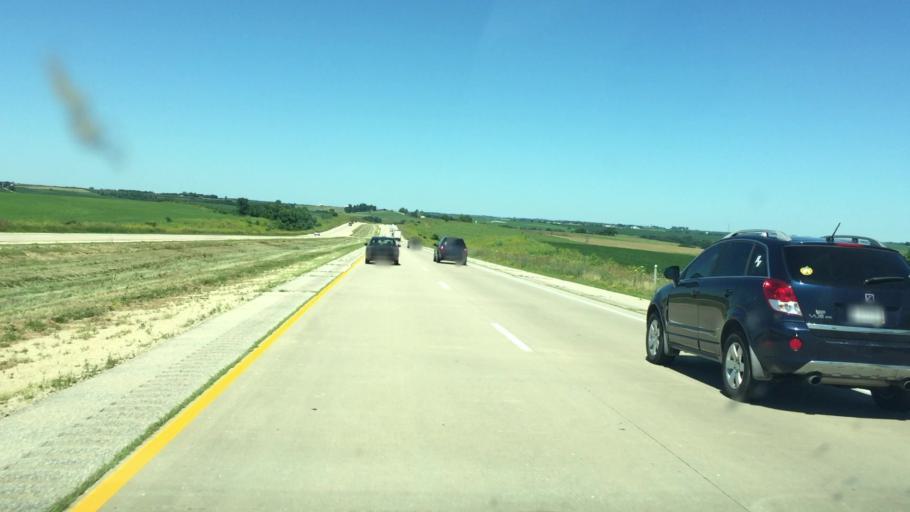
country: US
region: Wisconsin
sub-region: Iowa County
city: Mineral Point
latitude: 42.7989
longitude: -90.2783
